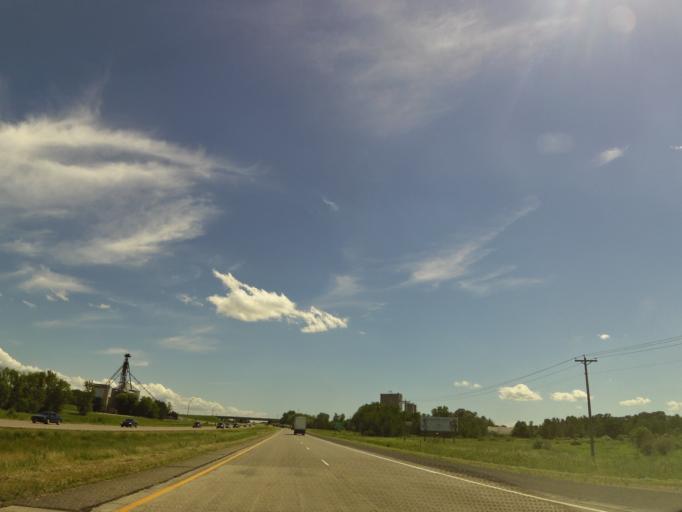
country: US
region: Minnesota
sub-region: Stearns County
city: Sartell
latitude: 45.6607
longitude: -94.1772
